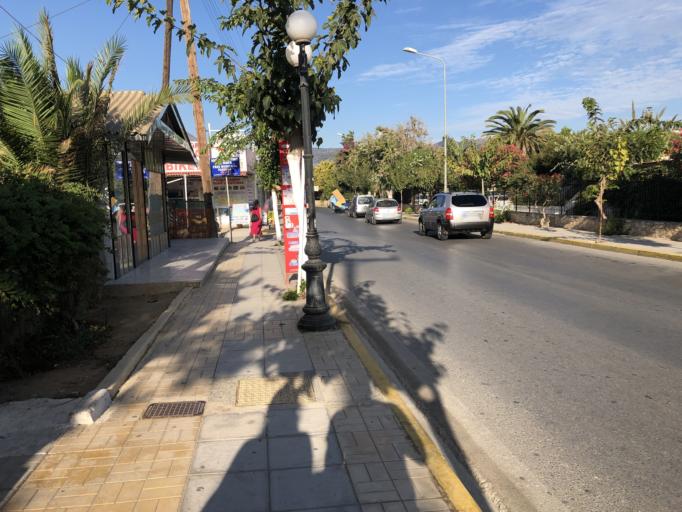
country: GR
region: Crete
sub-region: Nomos Irakleiou
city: Gazi
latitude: 35.3358
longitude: 25.0778
